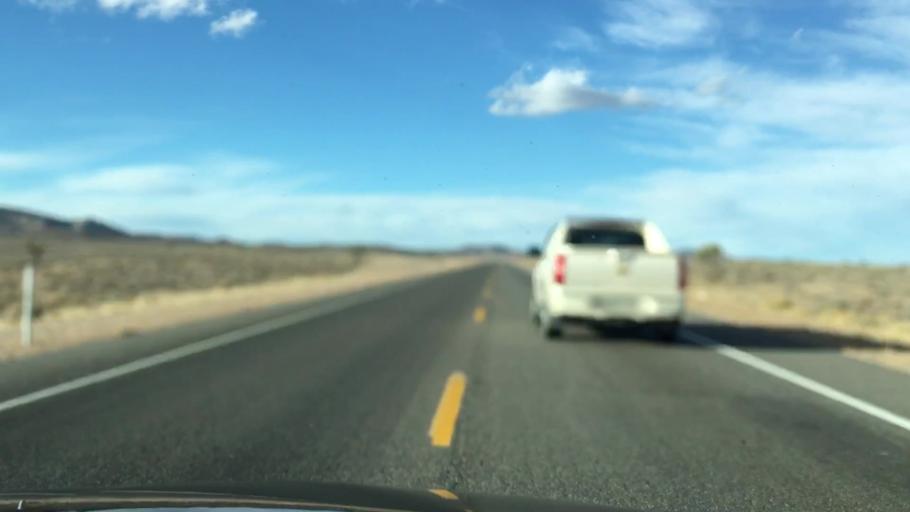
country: US
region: Nevada
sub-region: Esmeralda County
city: Goldfield
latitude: 37.5827
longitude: -117.2058
